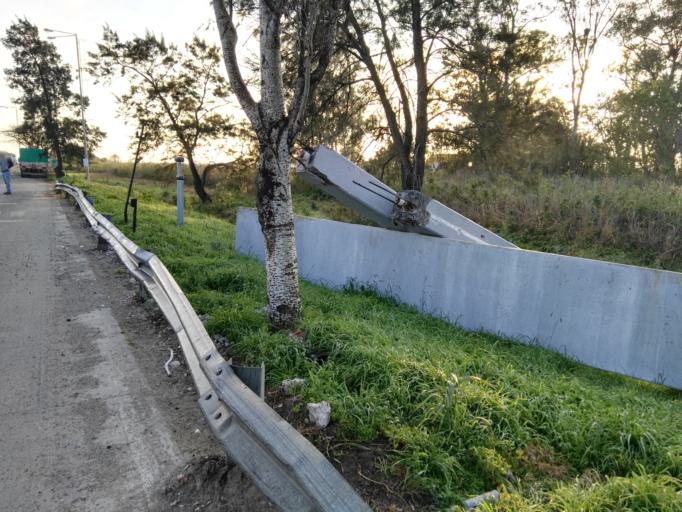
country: AR
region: Santa Fe
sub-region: Departamento de San Justo
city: San Justo
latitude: -30.9910
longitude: -60.6831
